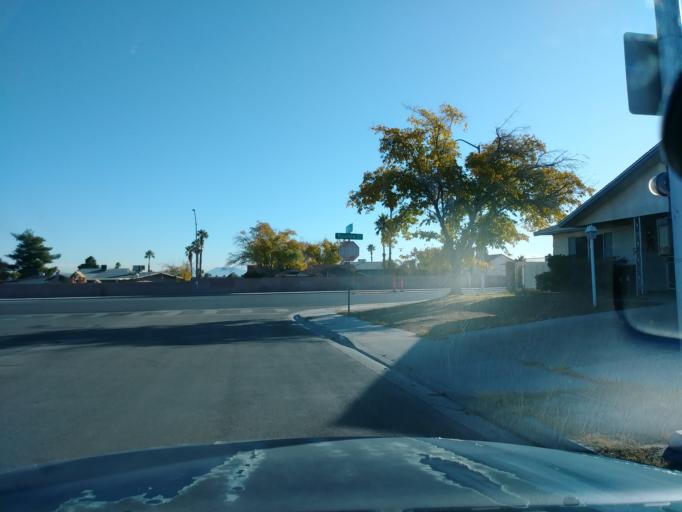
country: US
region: Nevada
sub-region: Clark County
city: Spring Valley
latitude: 36.1705
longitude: -115.2449
